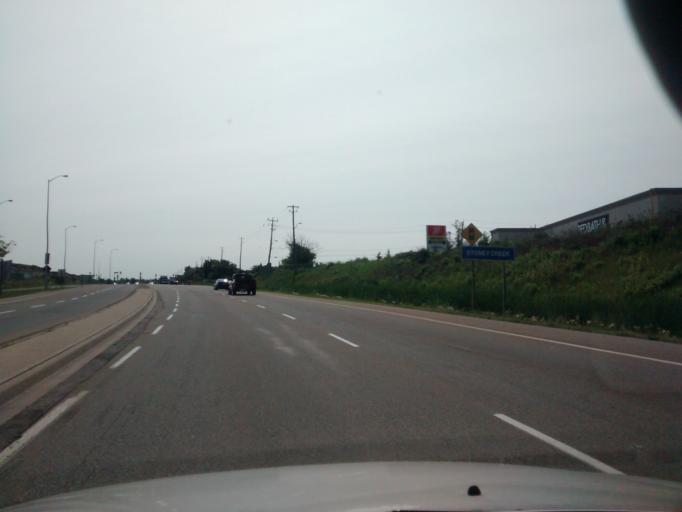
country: CA
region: Ontario
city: Hamilton
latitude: 43.1963
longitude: -79.8107
